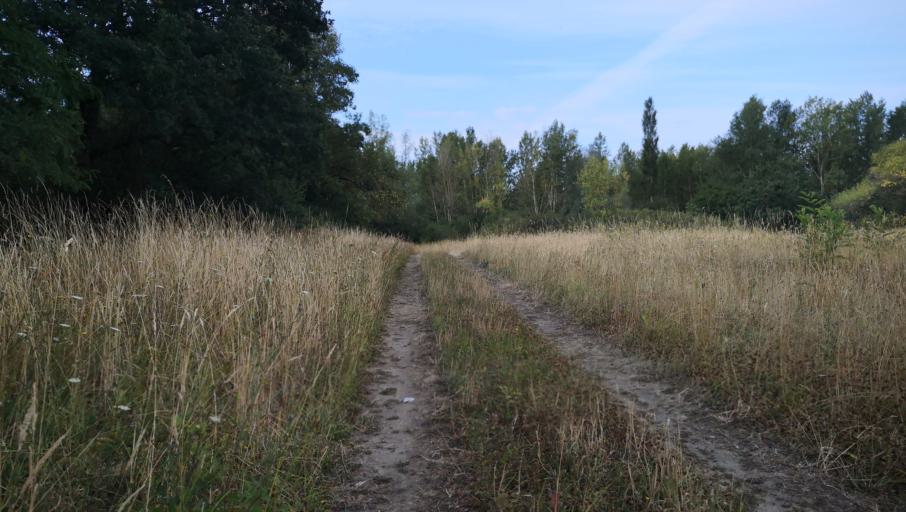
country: FR
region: Centre
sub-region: Departement du Loiret
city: Checy
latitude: 47.8930
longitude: 2.0036
